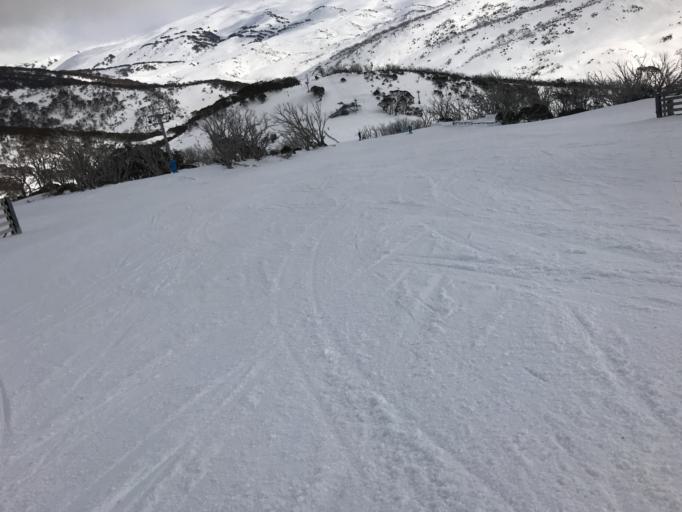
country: AU
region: New South Wales
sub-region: Snowy River
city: Jindabyne
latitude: -36.3814
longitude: 148.3834
